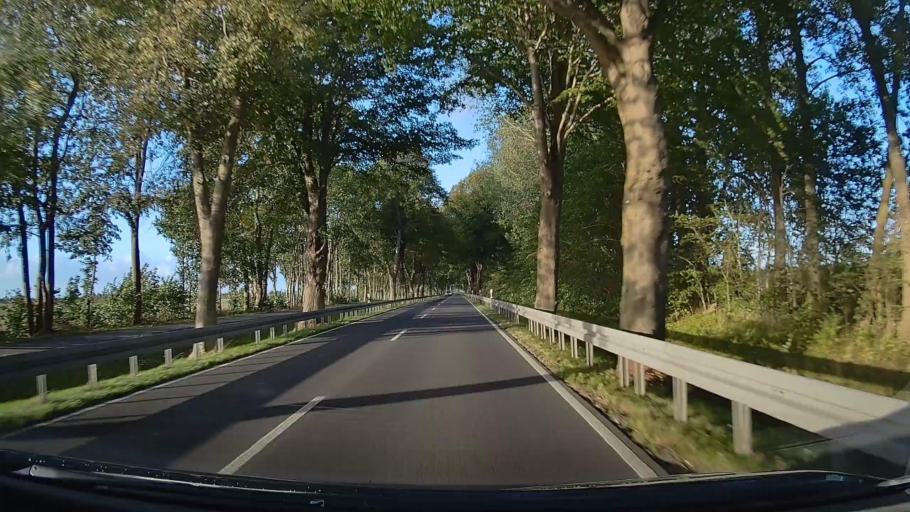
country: DE
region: Mecklenburg-Vorpommern
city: Wendorf
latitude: 54.2766
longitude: 13.0424
